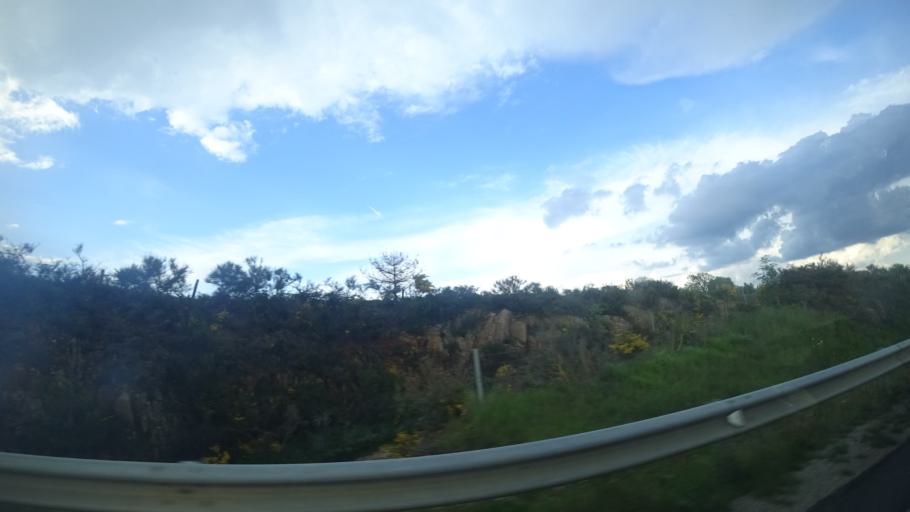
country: FR
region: Midi-Pyrenees
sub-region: Departement de l'Aveyron
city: Severac-le-Chateau
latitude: 44.2261
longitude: 2.9885
